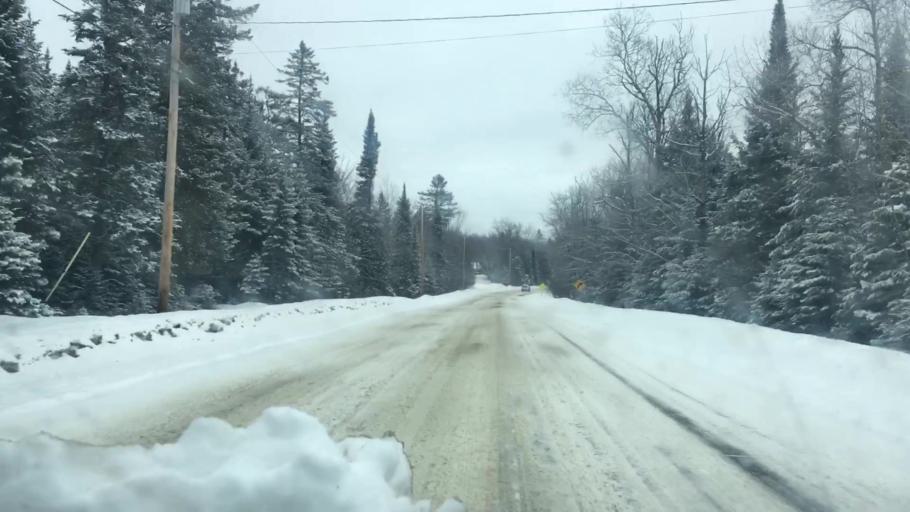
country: US
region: Maine
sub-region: Penobscot County
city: Bradford
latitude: 45.0320
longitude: -68.9516
